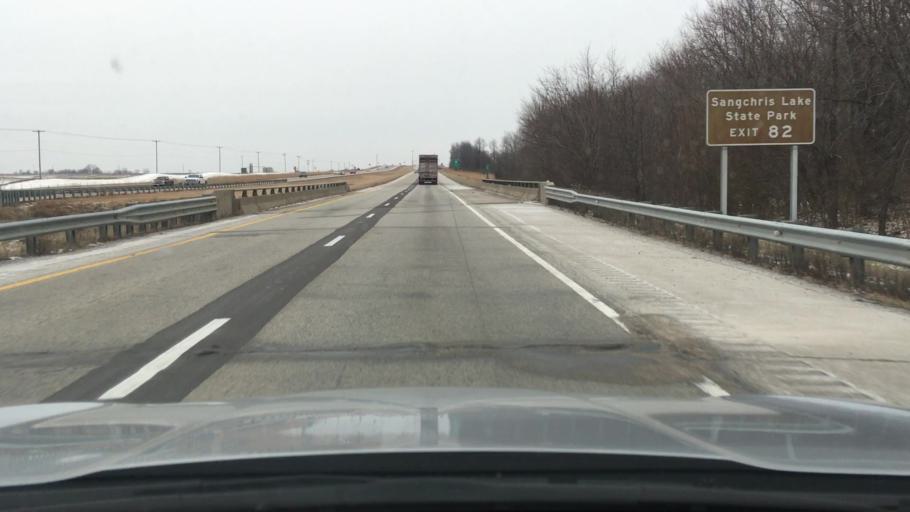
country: US
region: Illinois
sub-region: Sangamon County
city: Divernon
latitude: 39.5799
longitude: -89.6462
